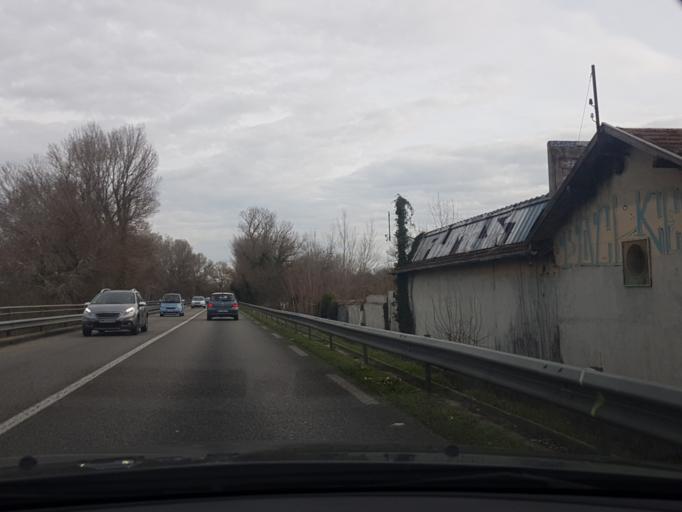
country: FR
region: Provence-Alpes-Cote d'Azur
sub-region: Departement du Vaucluse
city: Avignon
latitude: 43.9560
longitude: 4.8252
